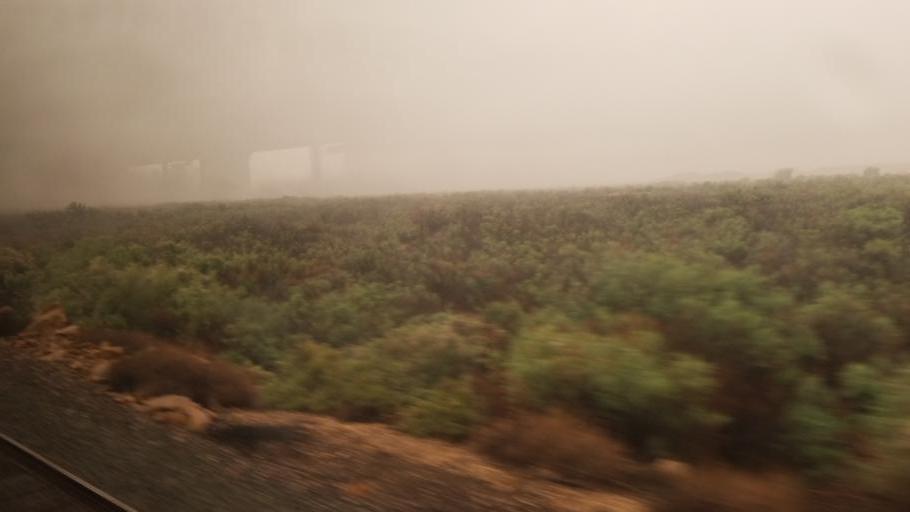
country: US
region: Arizona
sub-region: Navajo County
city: Joseph City
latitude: 34.9509
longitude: -110.3417
